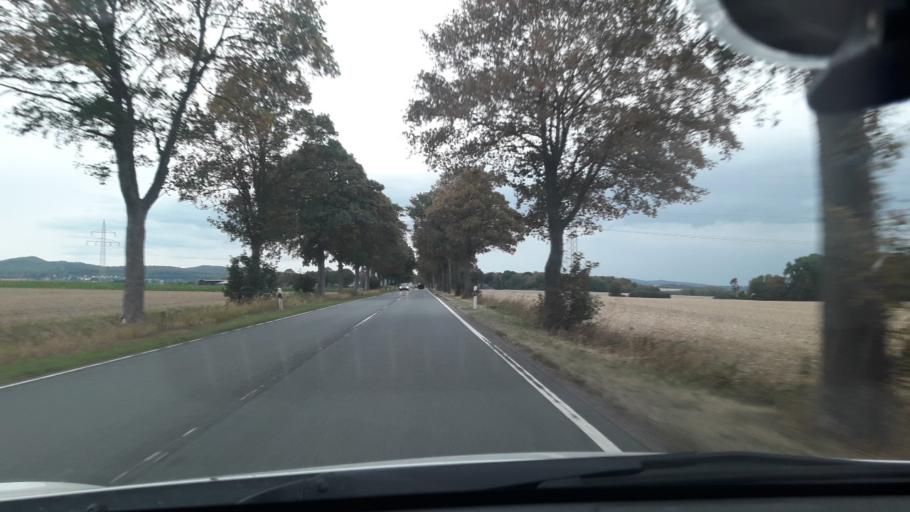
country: DE
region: Lower Saxony
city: Gielde
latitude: 52.0204
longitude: 10.4854
